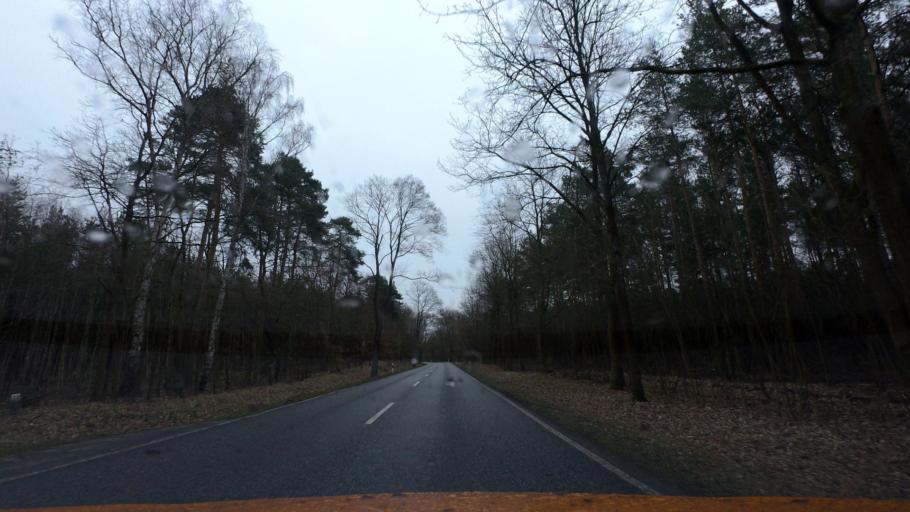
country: DE
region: Brandenburg
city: Falkensee
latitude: 52.6333
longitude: 13.0706
